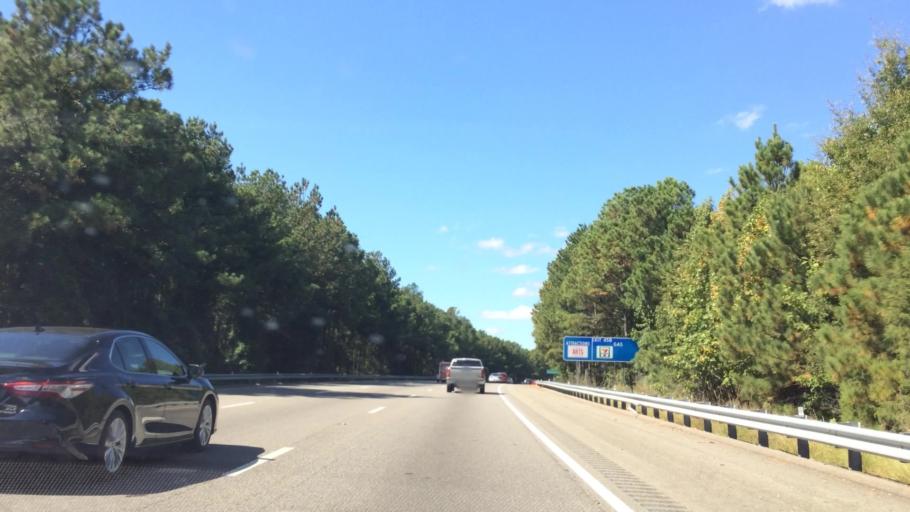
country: US
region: Virginia
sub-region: Henrico County
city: Glen Allen
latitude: 37.6607
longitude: -77.4713
